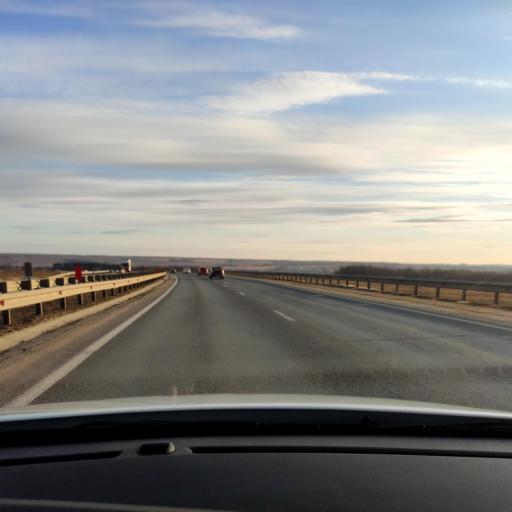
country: RU
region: Tatarstan
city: Vysokaya Gora
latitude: 55.7625
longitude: 49.3593
